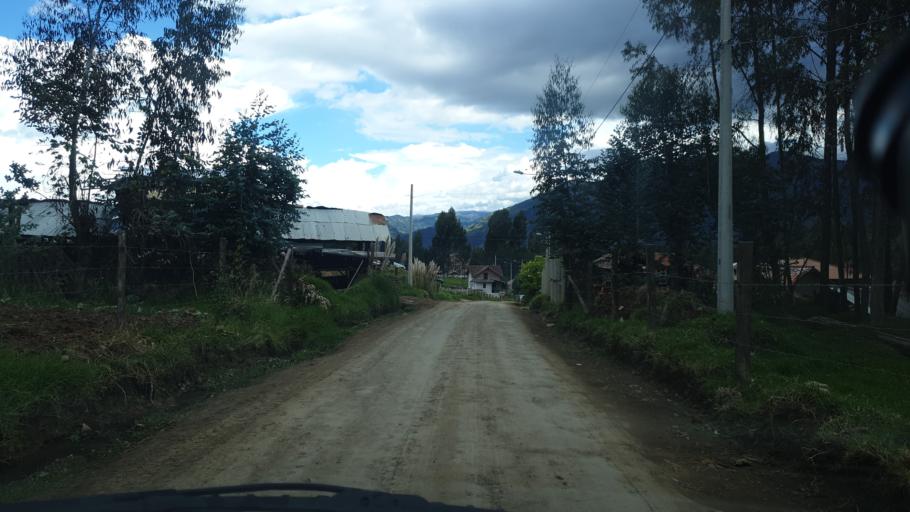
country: EC
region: Azuay
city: Cuenca
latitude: -2.8575
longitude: -79.0423
